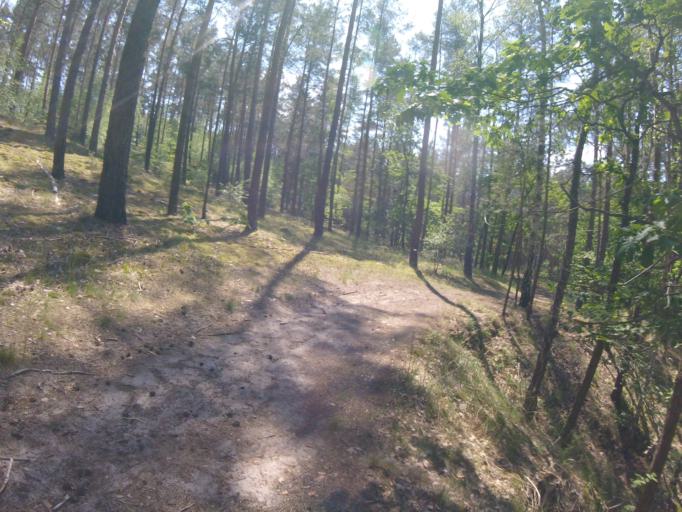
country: DE
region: Brandenburg
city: Teupitz
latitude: 52.1481
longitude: 13.5805
